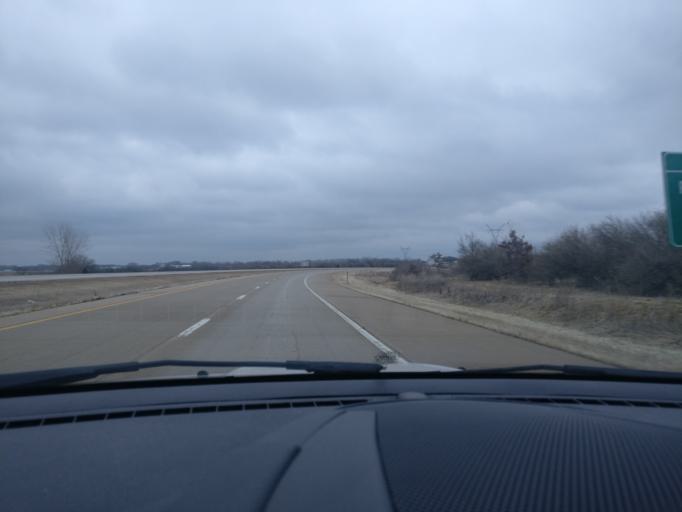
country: US
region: Illinois
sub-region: Whiteside County
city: Sterling
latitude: 41.7653
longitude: -89.8015
